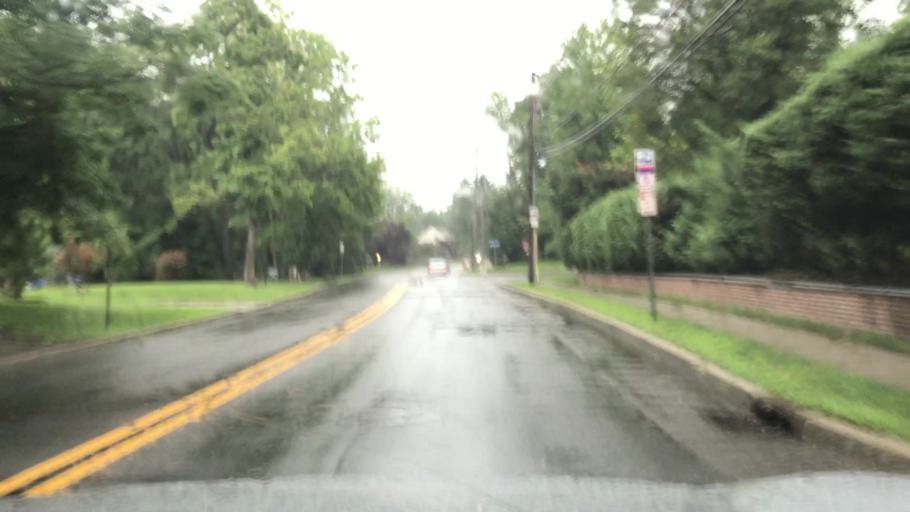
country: US
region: New Jersey
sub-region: Bergen County
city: Teaneck
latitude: 40.9093
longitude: -74.0235
